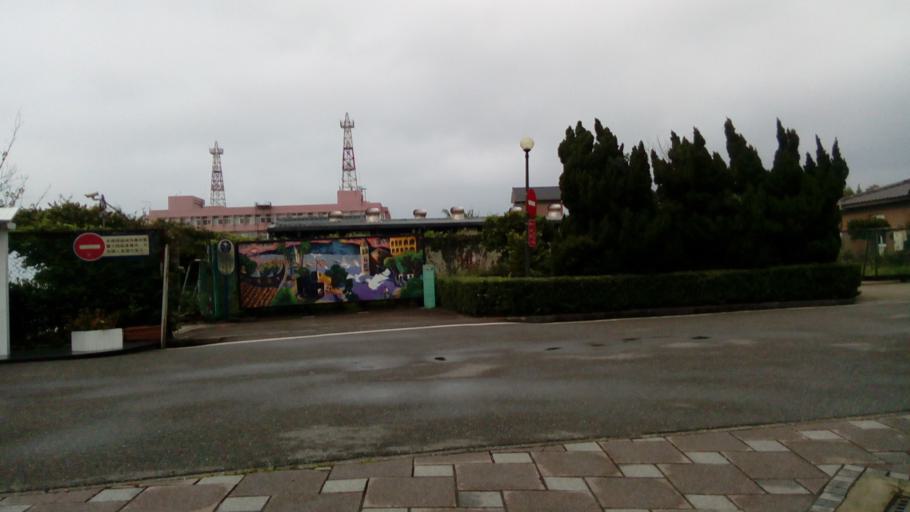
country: TW
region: Taipei
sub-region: Taipei
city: Banqiao
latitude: 25.1845
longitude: 121.4108
